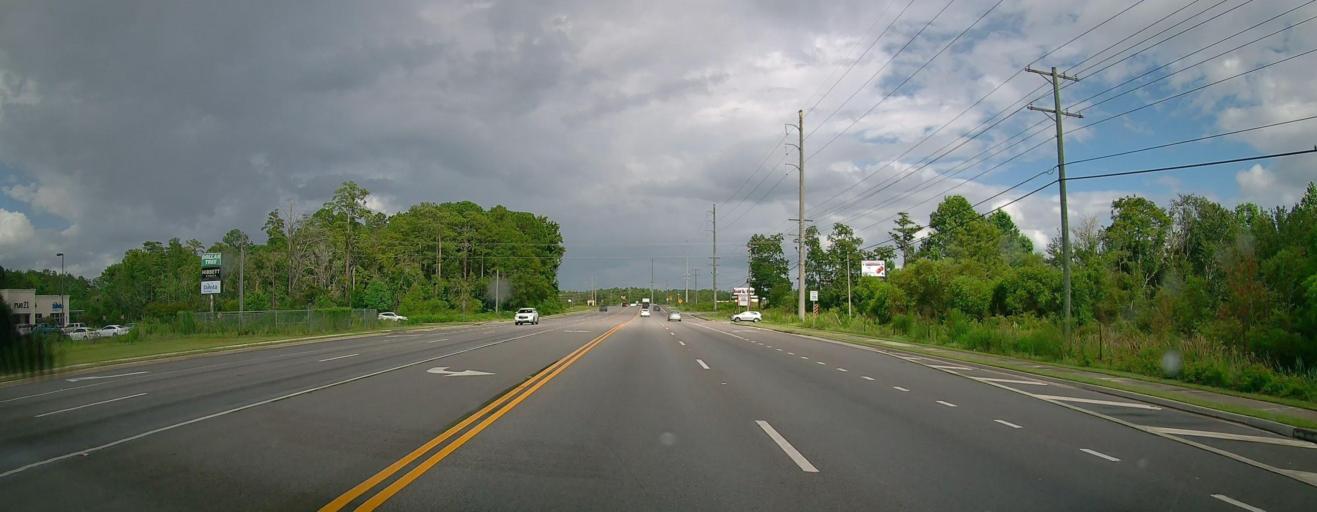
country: US
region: Georgia
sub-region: Coffee County
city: Douglas
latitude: 31.4876
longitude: -82.8465
